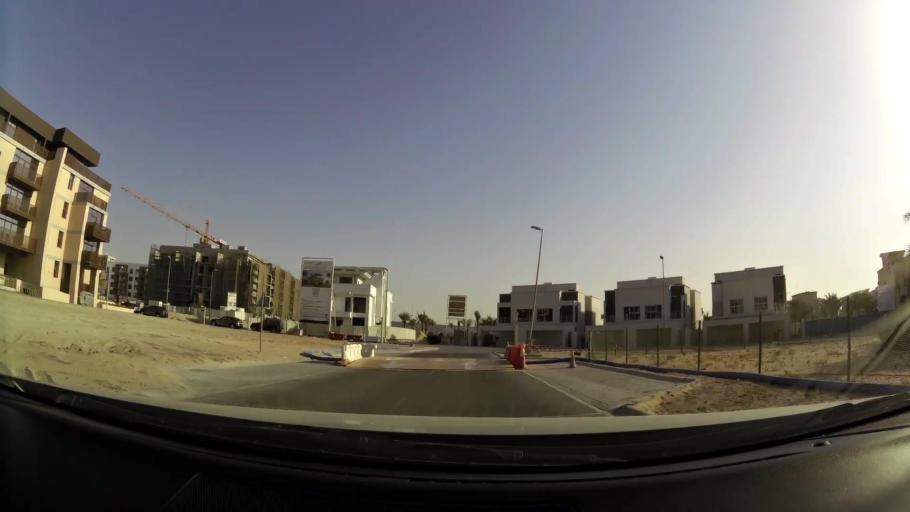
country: AE
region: Dubai
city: Dubai
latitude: 25.0478
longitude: 55.2028
